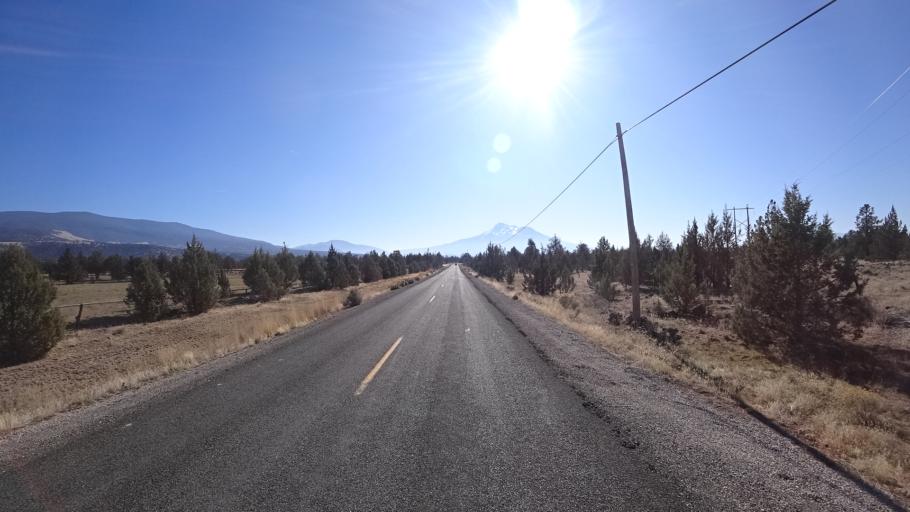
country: US
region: California
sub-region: Siskiyou County
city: Montague
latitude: 41.6552
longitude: -122.3633
